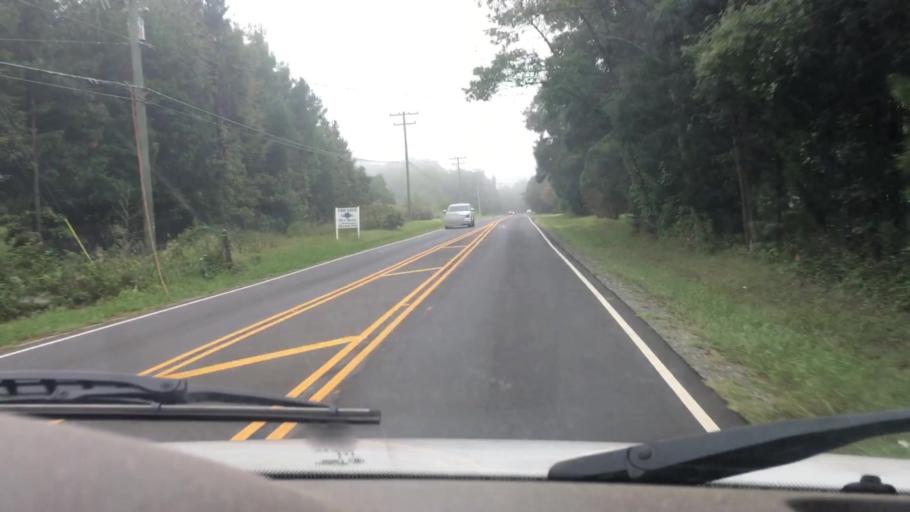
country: US
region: North Carolina
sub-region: Mecklenburg County
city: Huntersville
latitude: 35.3880
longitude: -80.7825
